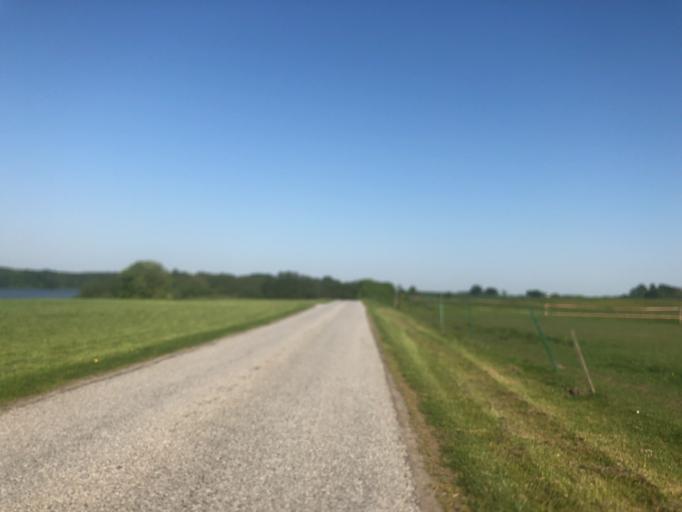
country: DK
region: Zealand
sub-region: Ringsted Kommune
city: Ringsted
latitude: 55.4815
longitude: 11.7782
